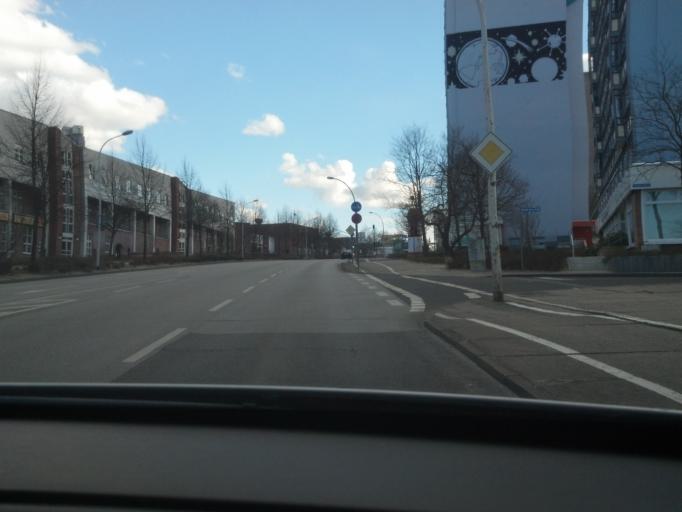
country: DE
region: Mecklenburg-Vorpommern
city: Neubrandenburg
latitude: 53.5558
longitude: 13.2920
